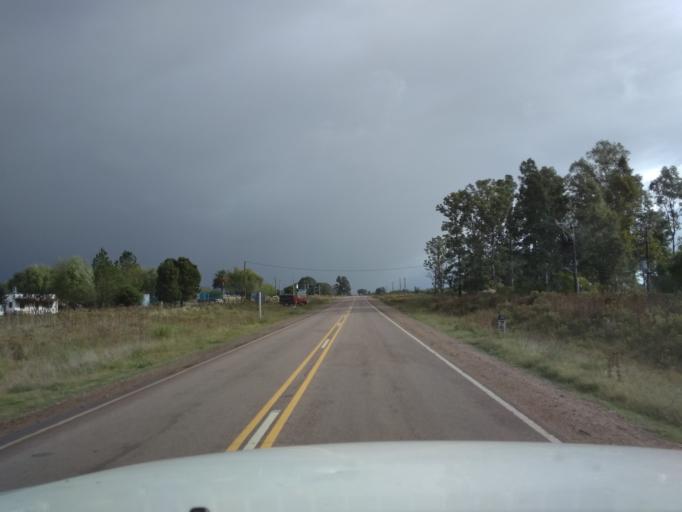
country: UY
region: Canelones
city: Tala
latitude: -34.3706
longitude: -55.7845
